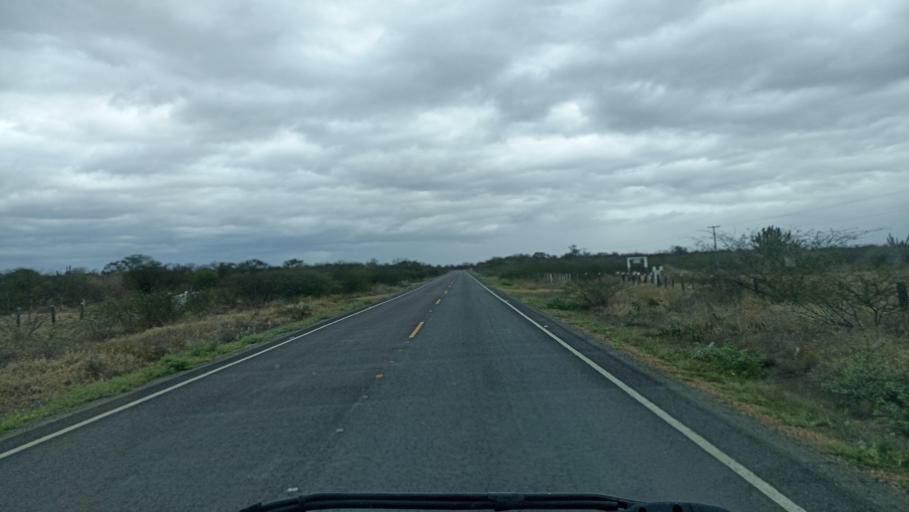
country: BR
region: Bahia
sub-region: Iacu
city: Iacu
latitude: -12.9766
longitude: -40.5131
